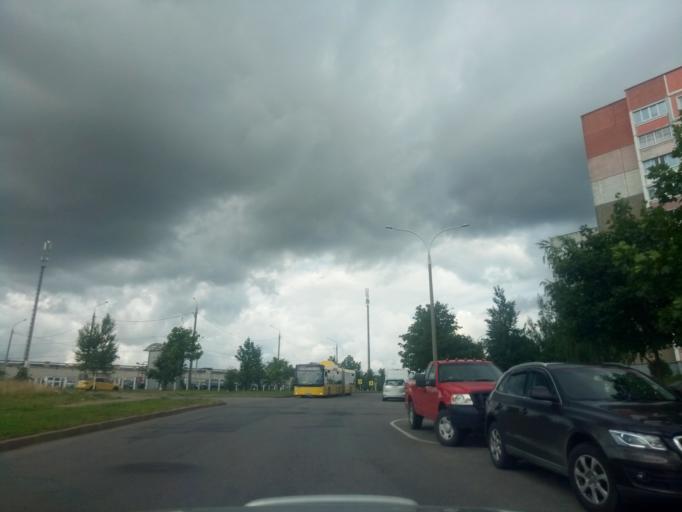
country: BY
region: Minsk
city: Malinovka
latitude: 53.8812
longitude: 27.4206
